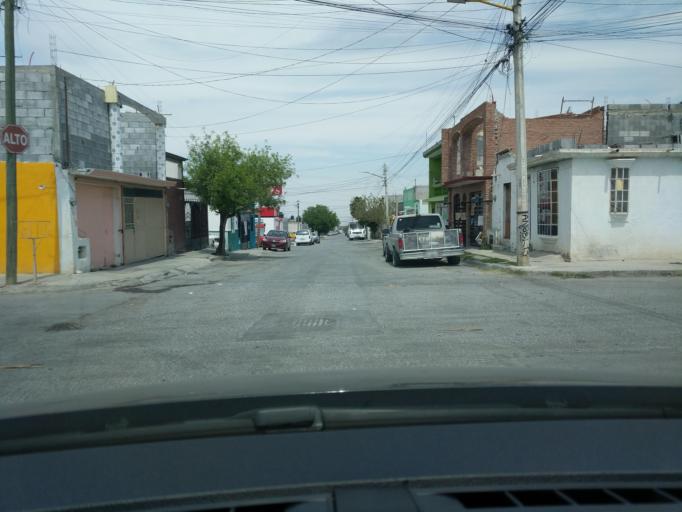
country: MX
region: Coahuila
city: Saltillo
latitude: 25.4081
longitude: -100.9381
